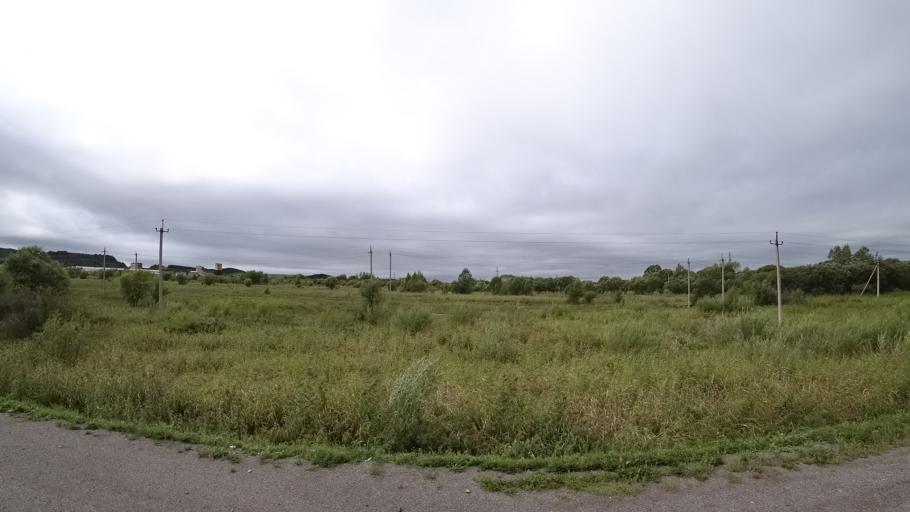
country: RU
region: Primorskiy
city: Monastyrishche
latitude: 44.1744
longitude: 132.4413
